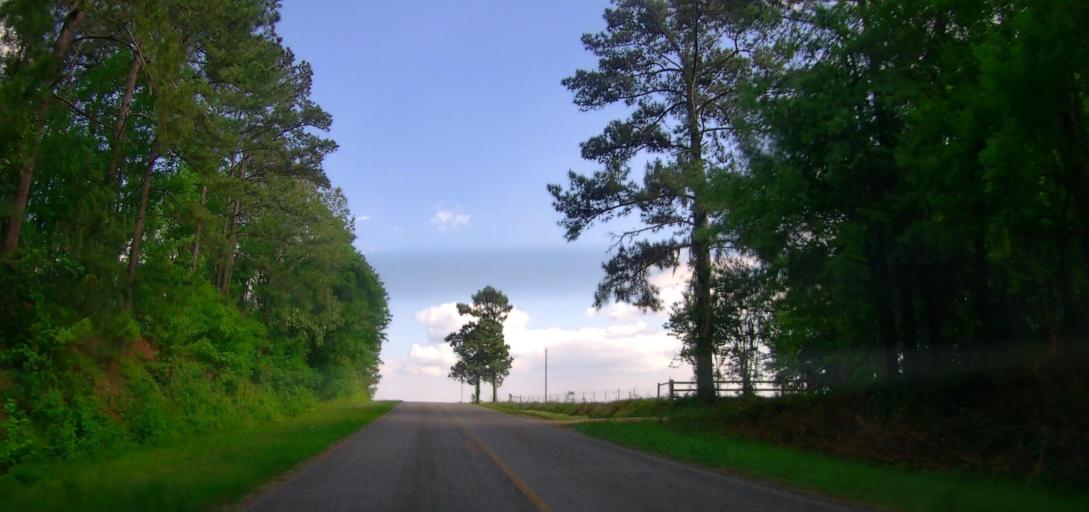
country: US
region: Georgia
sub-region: Laurens County
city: East Dublin
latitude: 32.6979
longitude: -82.9111
